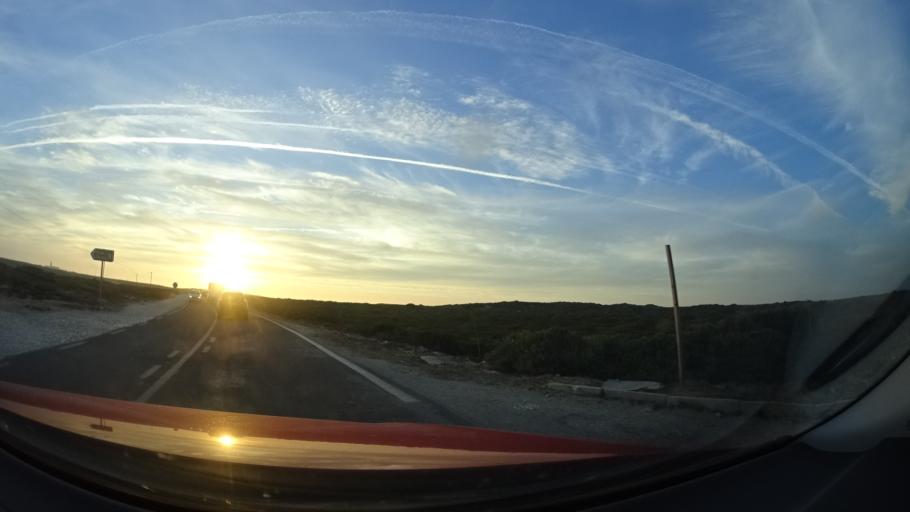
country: PT
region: Faro
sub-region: Vila do Bispo
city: Sagres
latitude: 37.0282
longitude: -8.9815
